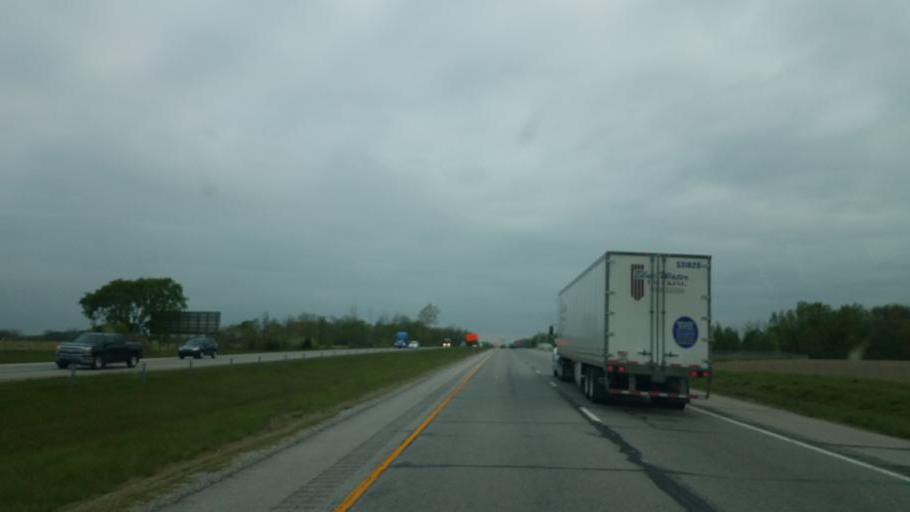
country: US
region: Indiana
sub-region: DeKalb County
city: Garrett
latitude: 41.2897
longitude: -85.0872
